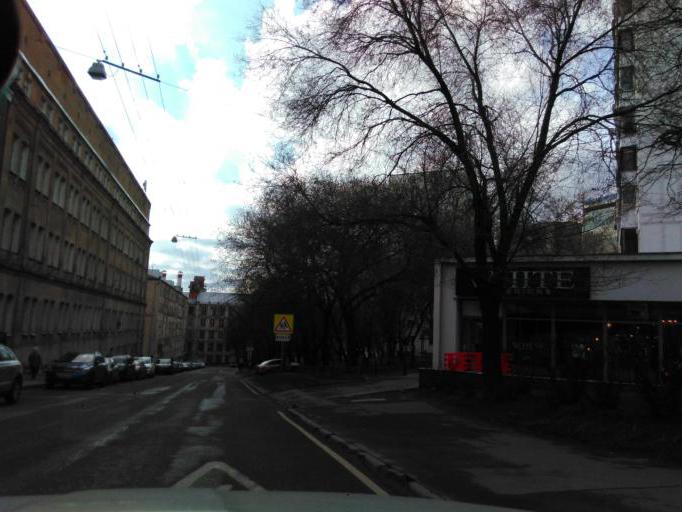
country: RU
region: Moskovskaya
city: Dorogomilovo
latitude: 55.7587
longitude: 37.5600
